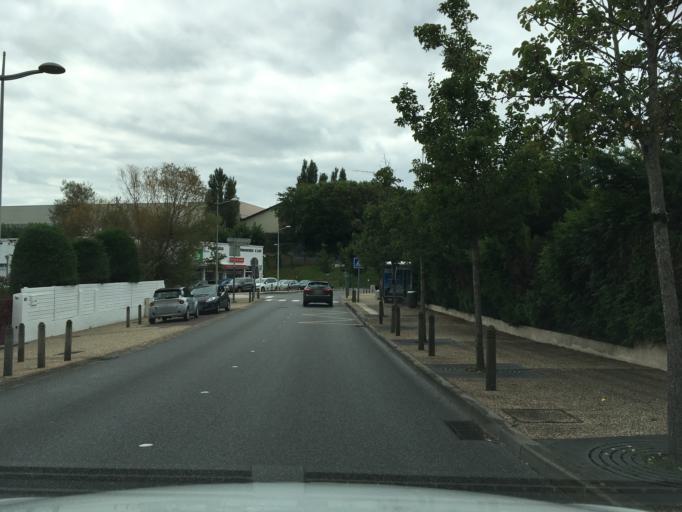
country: FR
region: Aquitaine
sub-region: Departement des Pyrenees-Atlantiques
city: Anglet
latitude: 43.5032
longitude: -1.5036
